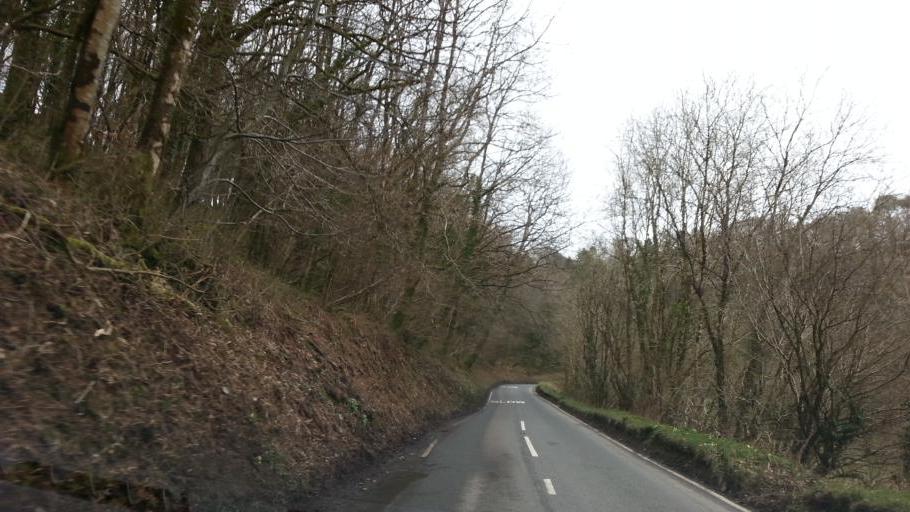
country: GB
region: England
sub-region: Devon
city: Combe Martin
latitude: 51.1445
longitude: -4.0043
